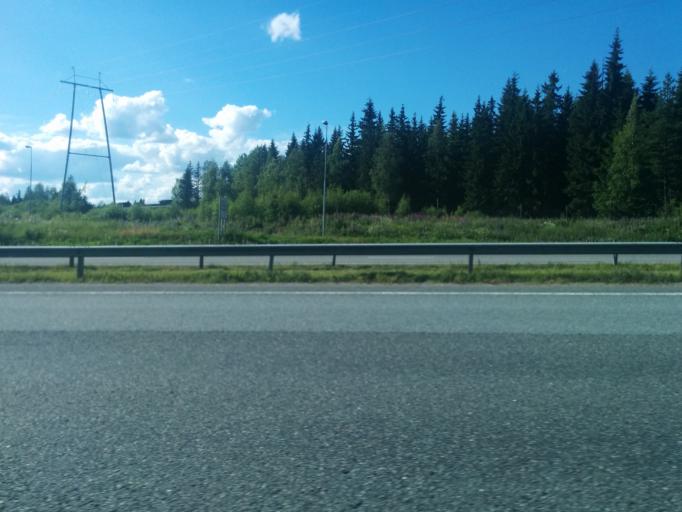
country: FI
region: Pirkanmaa
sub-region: Tampere
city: Tampere
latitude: 61.4994
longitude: 23.8876
